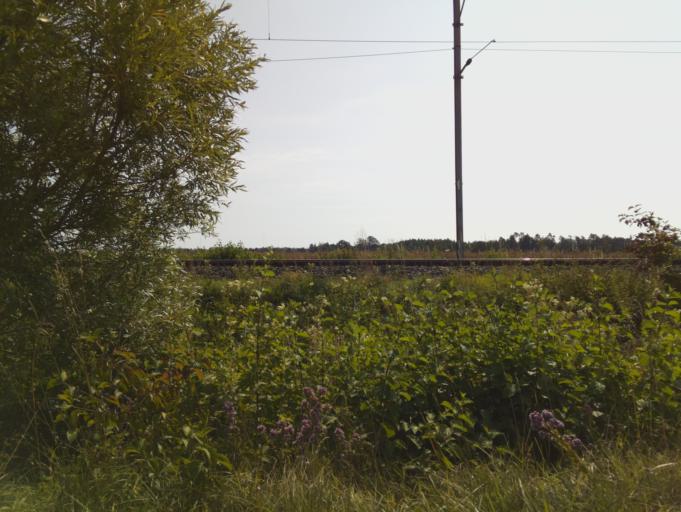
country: CH
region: Zurich
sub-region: Bezirk Andelfingen
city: Henggart
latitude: 47.5721
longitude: 8.6823
